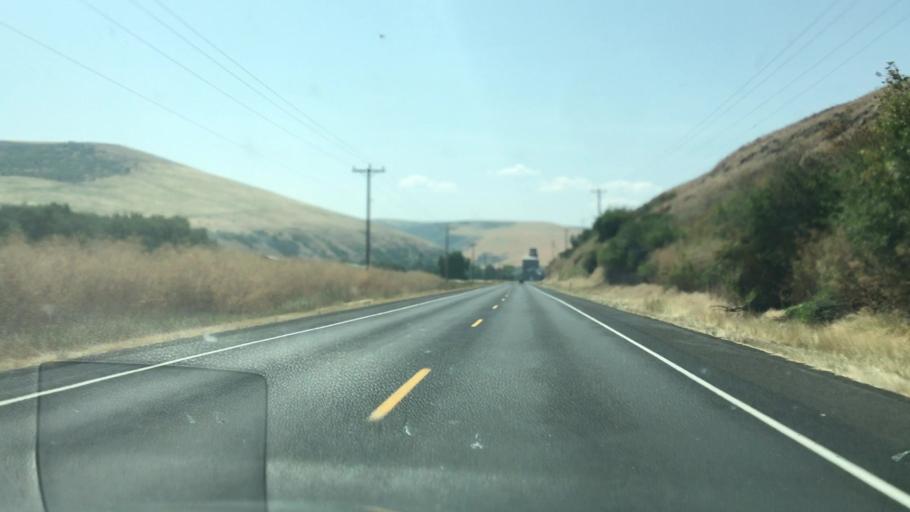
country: US
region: Idaho
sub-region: Nez Perce County
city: Lapwai
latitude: 46.3814
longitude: -116.7962
